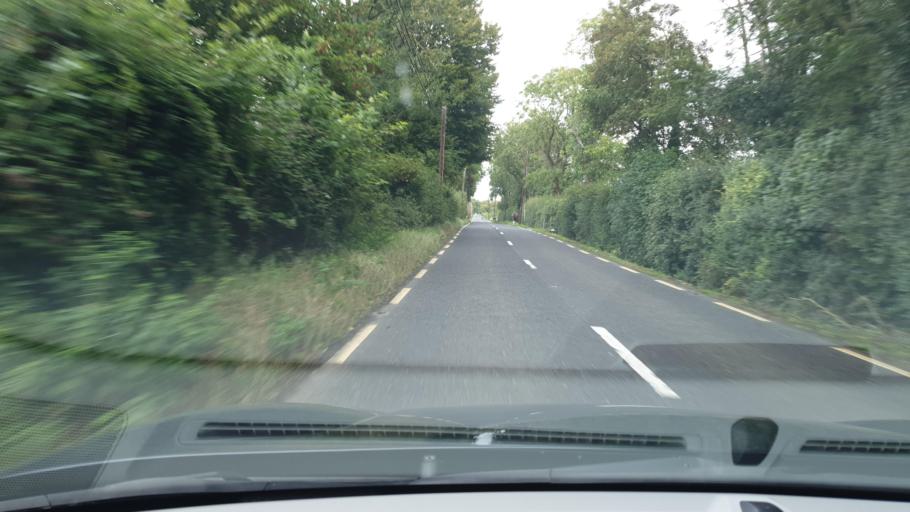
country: IE
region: Leinster
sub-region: Kildare
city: Maynooth
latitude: 53.3600
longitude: -6.6313
